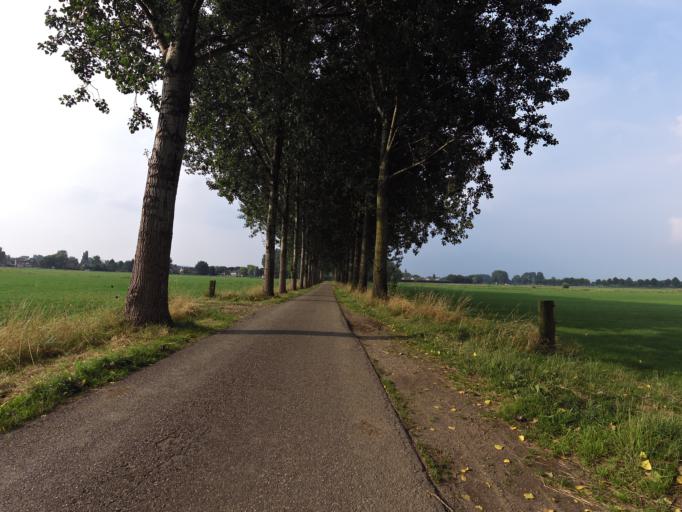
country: NL
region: Gelderland
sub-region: Gemeente Rheden
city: De Steeg
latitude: 51.9880
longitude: 6.0683
